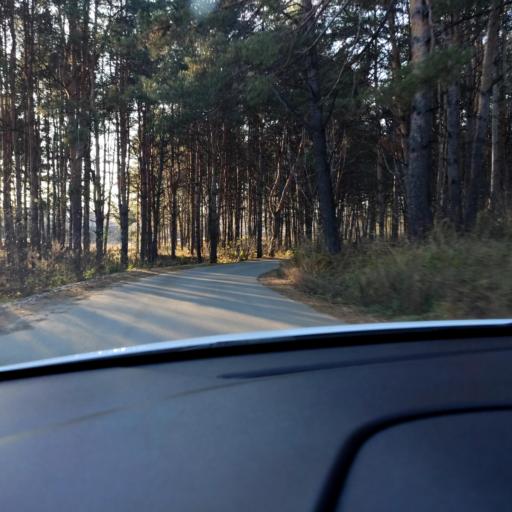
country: RU
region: Tatarstan
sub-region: Gorod Kazan'
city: Kazan
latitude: 55.8855
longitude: 49.0664
